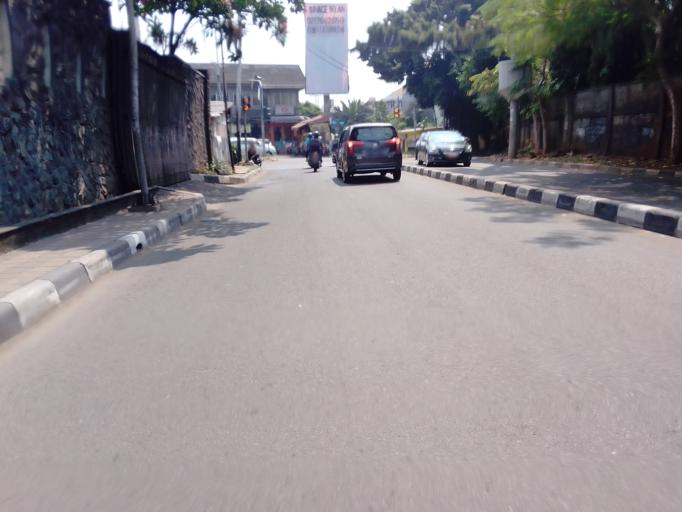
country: ID
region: Jakarta Raya
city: Jakarta
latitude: -6.2191
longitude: 106.7953
